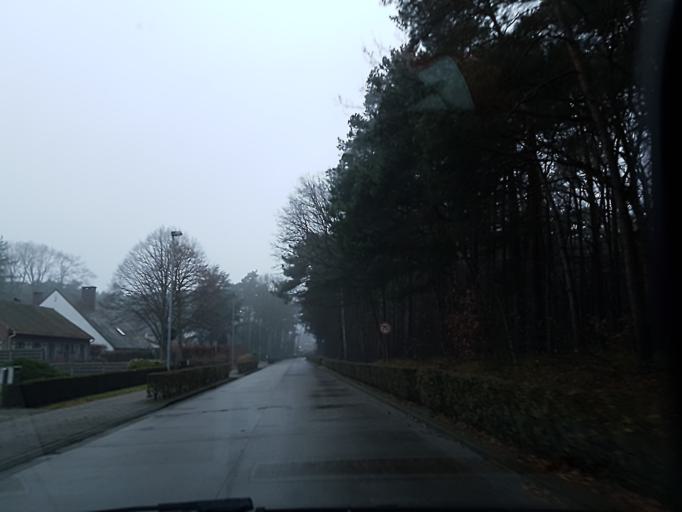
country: BE
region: Flanders
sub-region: Provincie Vlaams-Brabant
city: Boortmeerbeek
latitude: 51.0087
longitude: 4.5880
